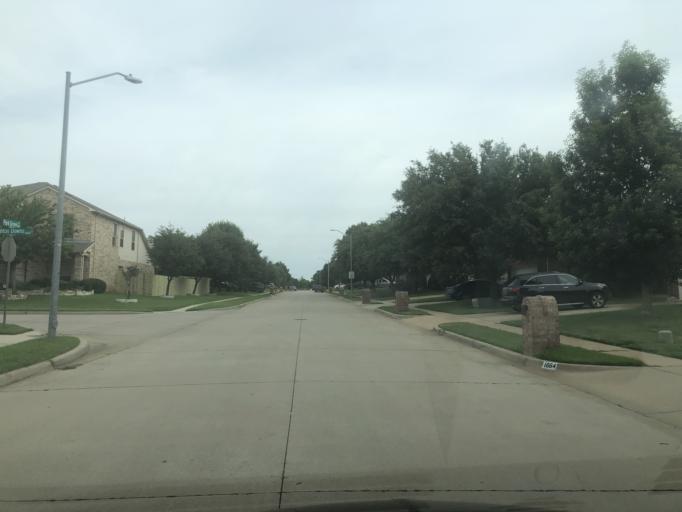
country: US
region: Texas
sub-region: Dallas County
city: Irving
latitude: 32.7952
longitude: -96.9865
